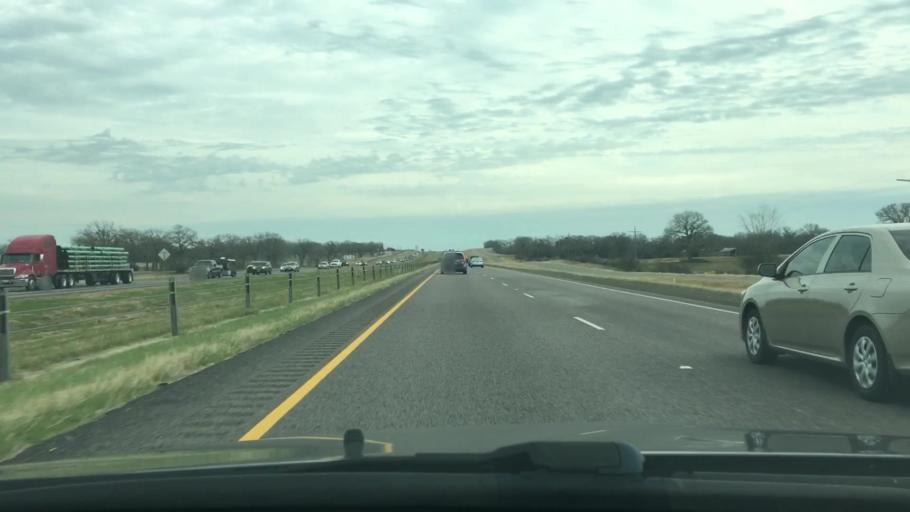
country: US
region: Texas
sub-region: Madison County
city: Madisonville
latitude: 30.9564
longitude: -95.8719
